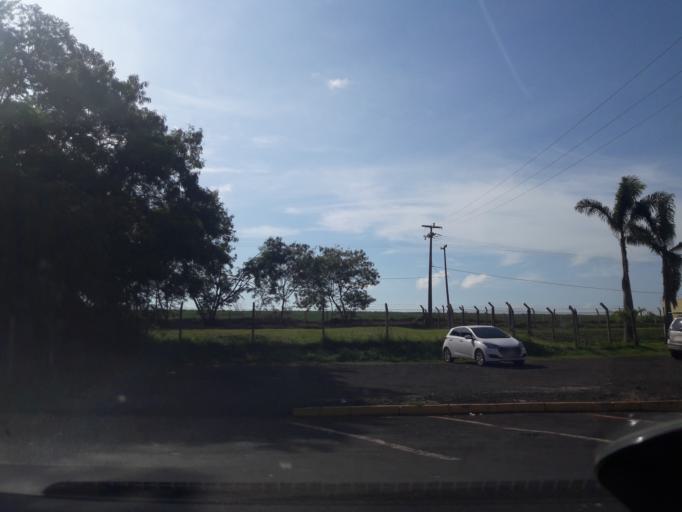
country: BR
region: Parana
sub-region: Paicandu
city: Paicandu
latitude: -23.6357
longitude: -52.1068
